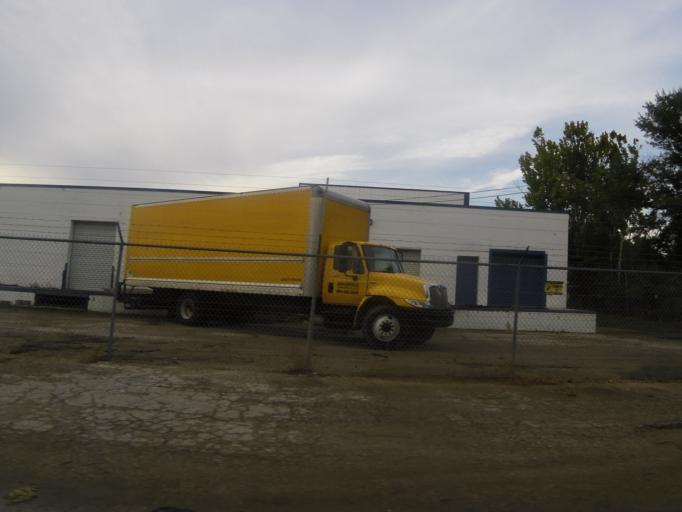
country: US
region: Florida
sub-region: Duval County
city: Jacksonville
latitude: 30.3300
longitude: -81.7046
